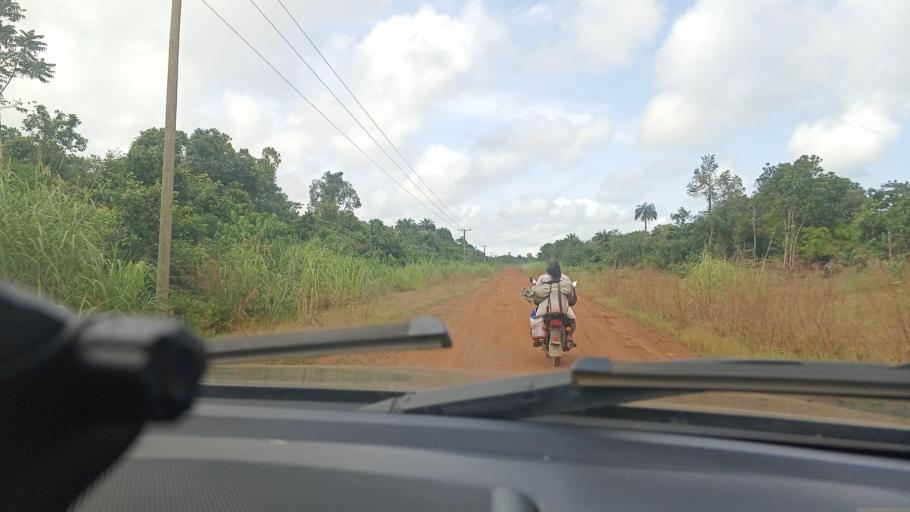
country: LR
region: Grand Cape Mount
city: Robertsport
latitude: 6.6823
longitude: -11.1305
